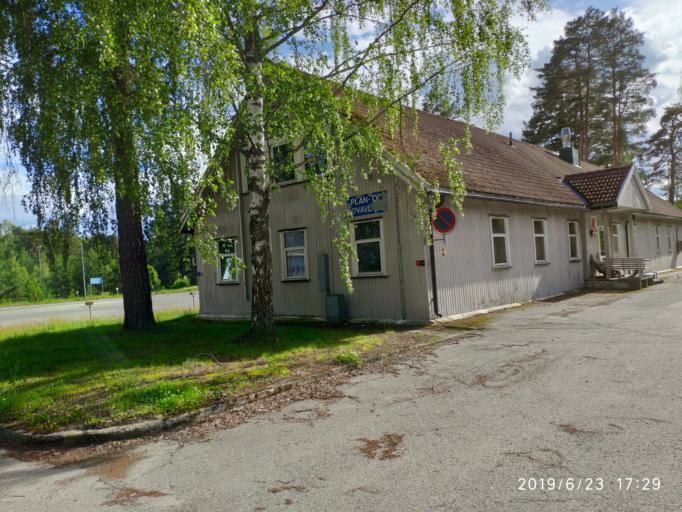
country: NO
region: Buskerud
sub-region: Ringerike
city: Honefoss
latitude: 60.1911
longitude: 10.2897
